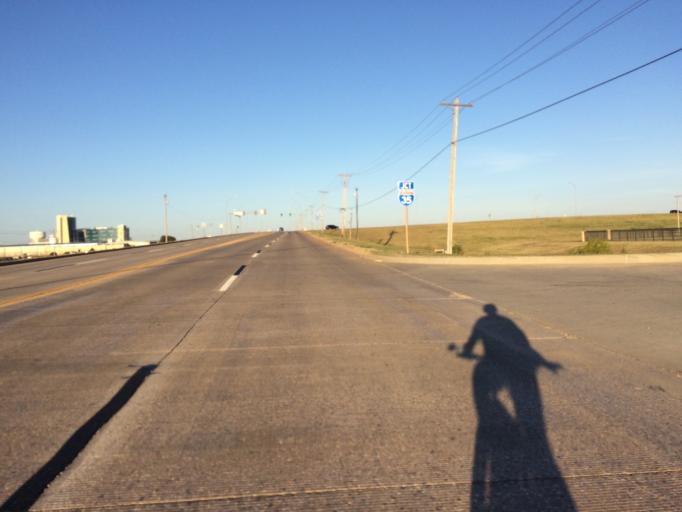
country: US
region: Oklahoma
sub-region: Cleveland County
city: Norman
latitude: 35.2621
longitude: -97.4811
